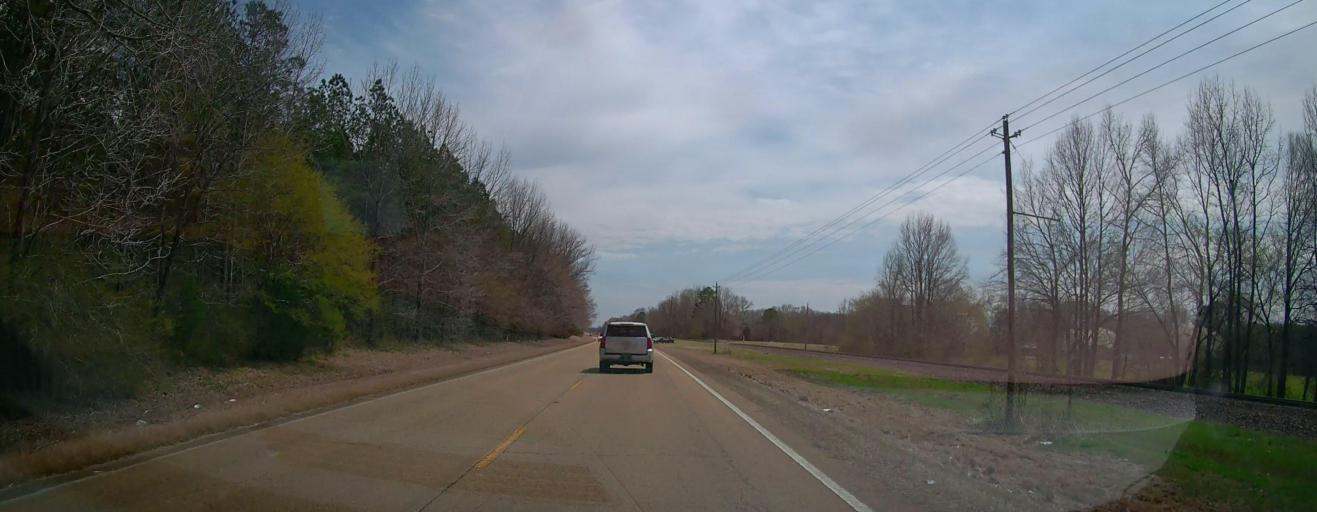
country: US
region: Mississippi
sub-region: Benton County
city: Ashland
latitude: 34.6271
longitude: -89.2607
